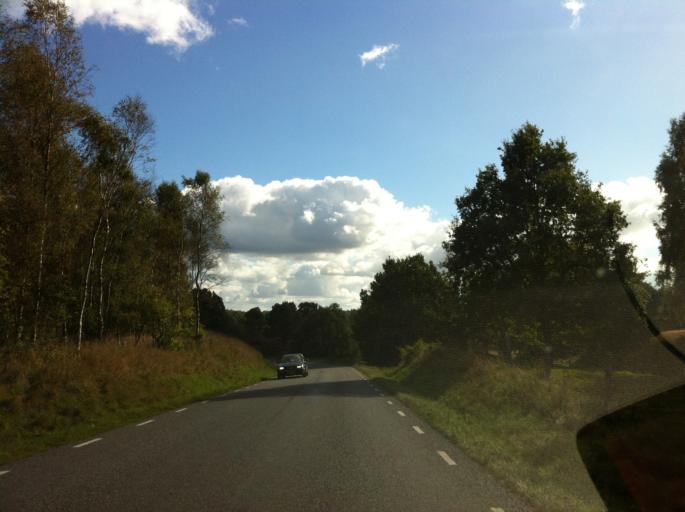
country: SE
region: Skane
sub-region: Kristianstads Kommun
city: Degeberga
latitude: 55.7124
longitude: 13.9779
